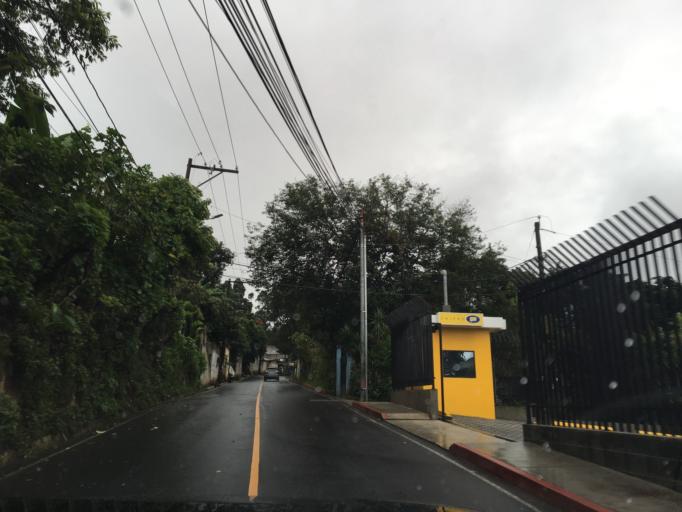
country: GT
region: Guatemala
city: Santa Catarina Pinula
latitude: 14.5614
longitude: -90.4995
